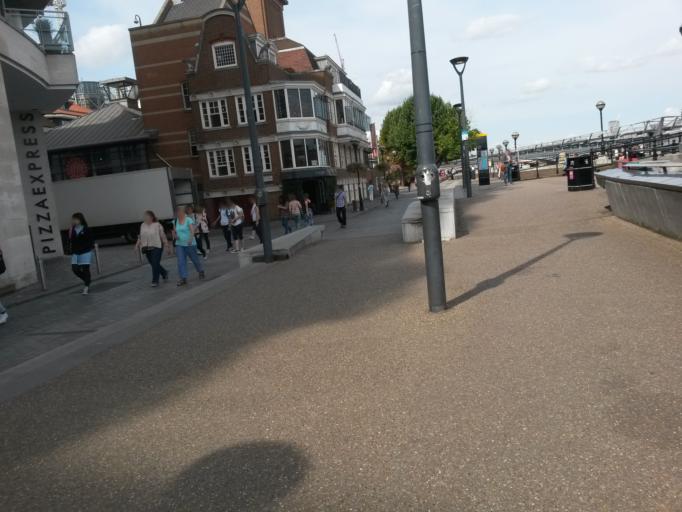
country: GB
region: England
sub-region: Greater London
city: City of London
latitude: 51.5083
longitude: -0.0959
